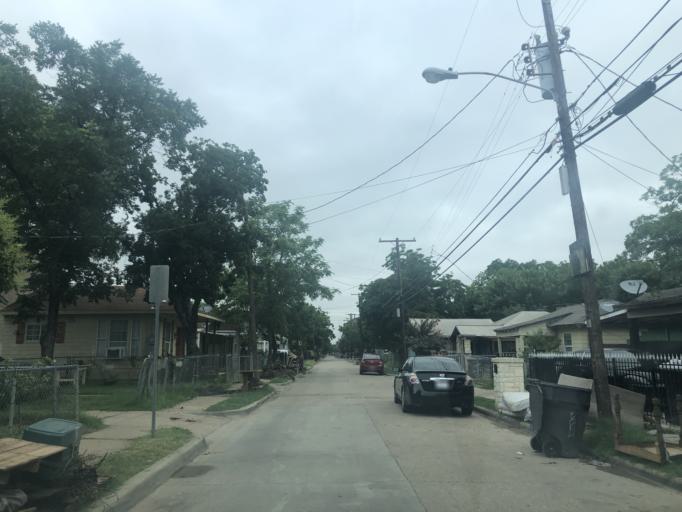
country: US
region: Texas
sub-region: Dallas County
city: Dallas
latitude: 32.7789
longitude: -96.8456
